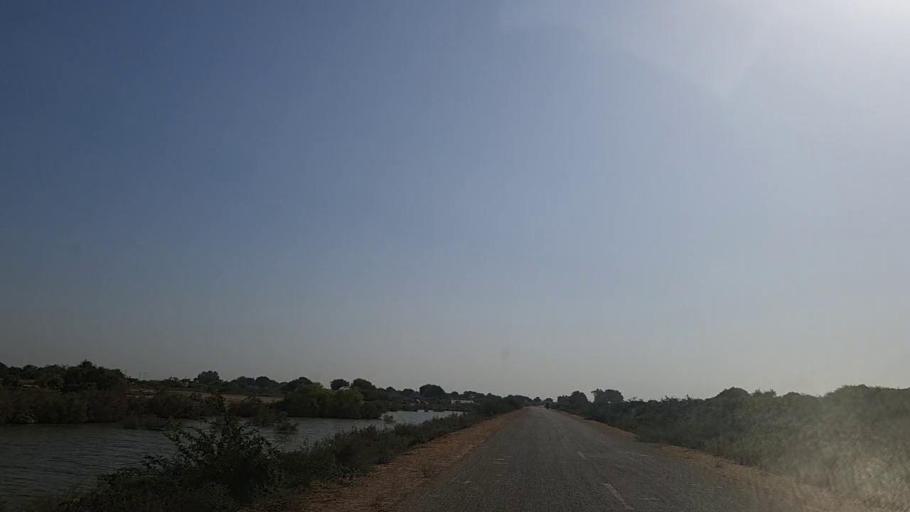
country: PK
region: Sindh
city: Jati
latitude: 24.4296
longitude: 68.2588
